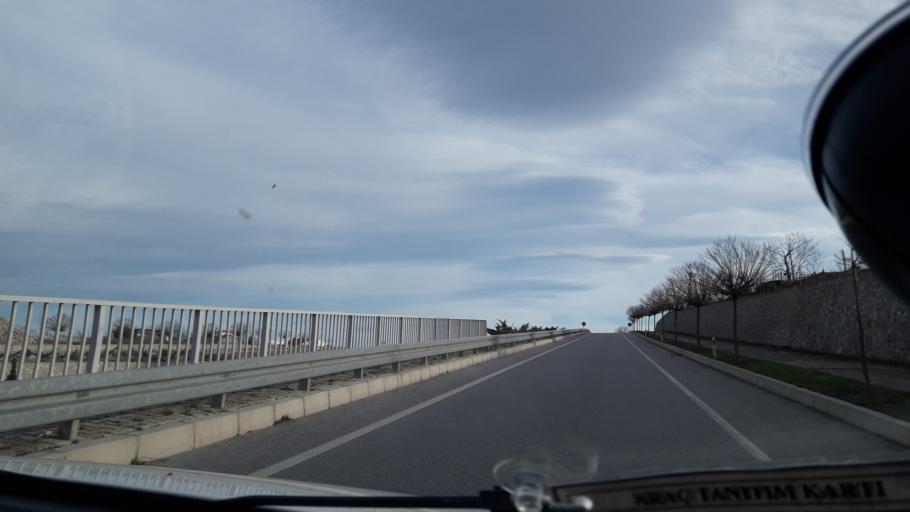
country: TR
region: Sinop
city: Gerze
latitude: 41.8028
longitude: 35.1765
